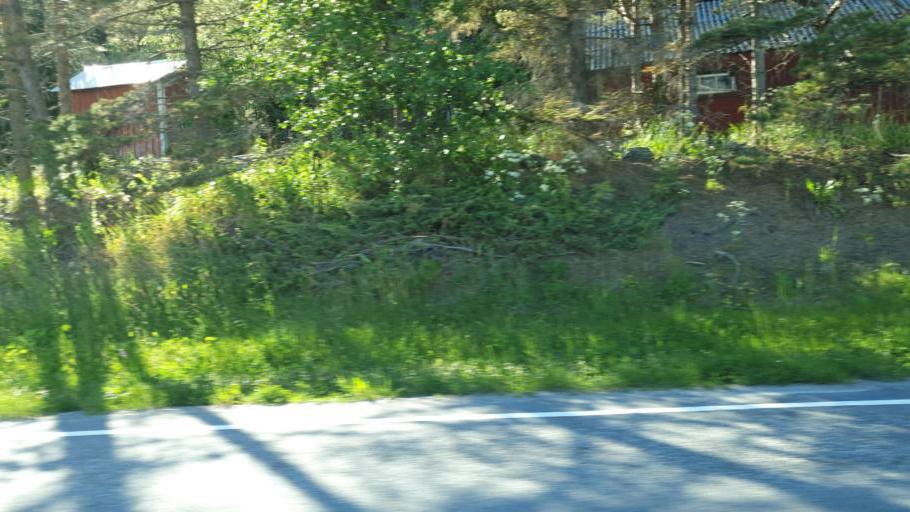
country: NO
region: Sor-Trondelag
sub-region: Skaun
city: Borsa
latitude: 63.5040
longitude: 10.1295
